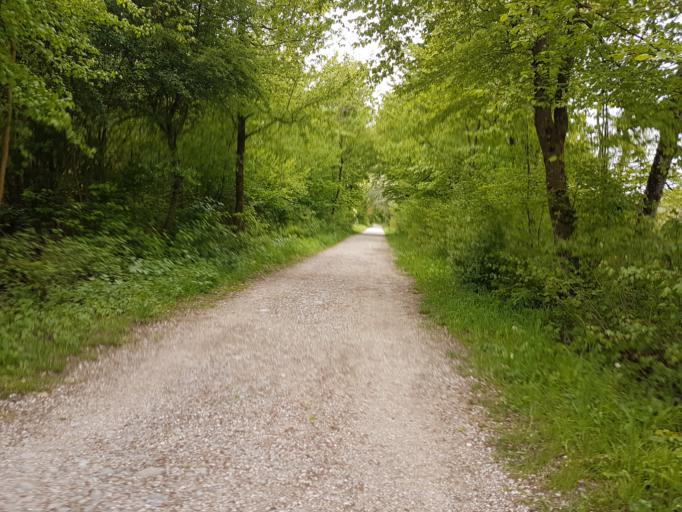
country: CH
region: Bern
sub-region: Oberaargau
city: Aarwangen
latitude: 47.2266
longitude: 7.7280
